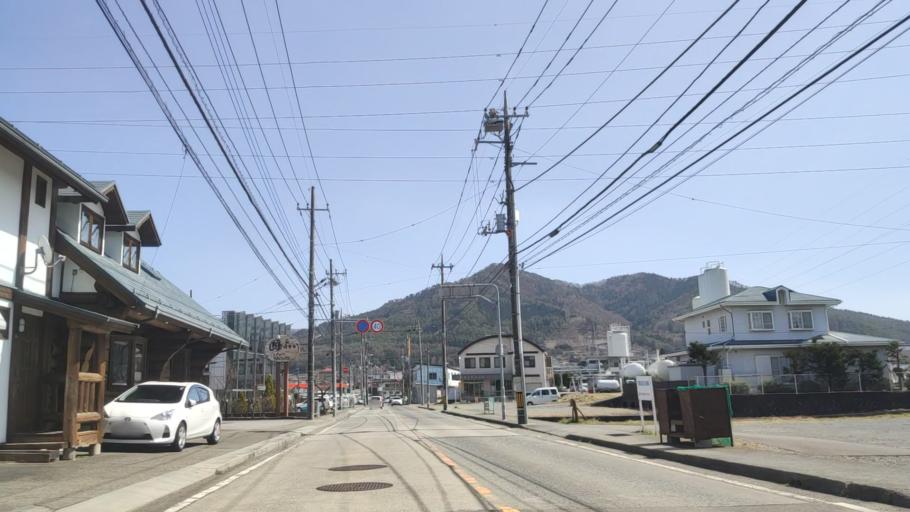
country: JP
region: Yamanashi
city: Fujikawaguchiko
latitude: 35.4866
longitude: 138.8100
